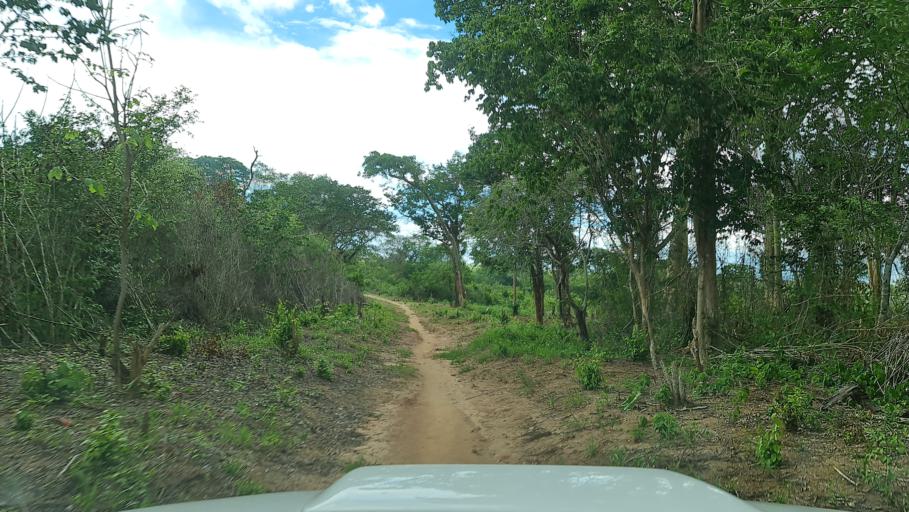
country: MZ
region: Nampula
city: Ilha de Mocambique
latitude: -15.4980
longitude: 40.1671
